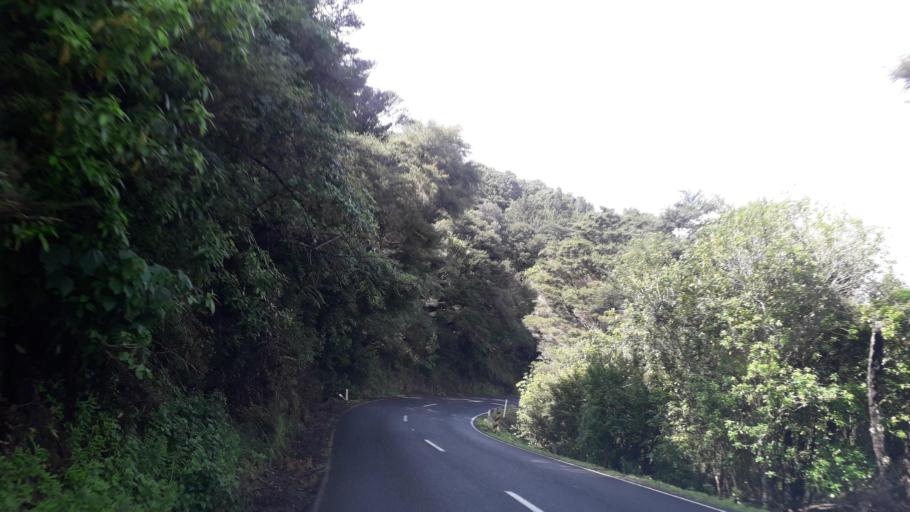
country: NZ
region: Northland
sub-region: Far North District
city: Paihia
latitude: -35.2525
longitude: 174.2626
